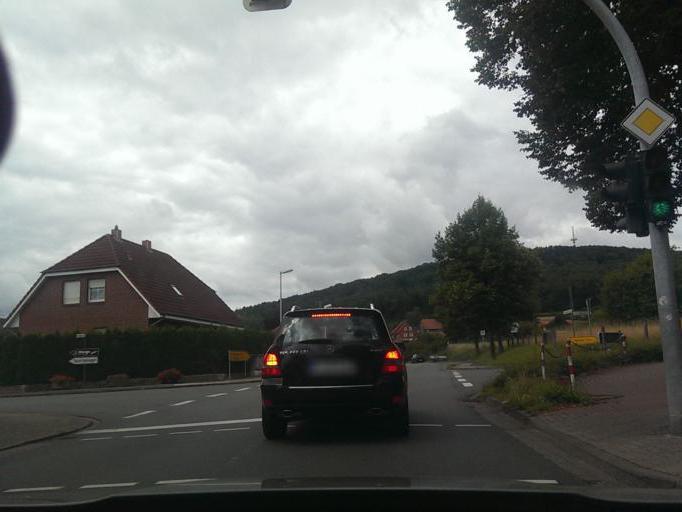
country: DE
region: Lower Saxony
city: Alfeld
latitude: 51.9667
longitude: 9.8020
